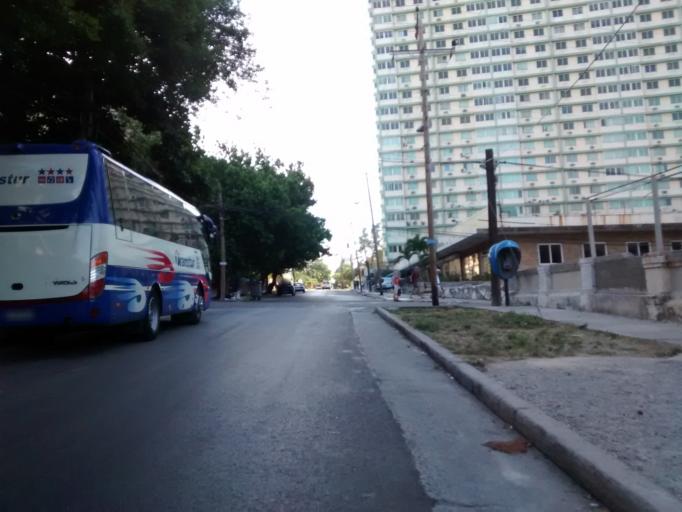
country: CU
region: La Habana
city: Havana
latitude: 23.1430
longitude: -82.3831
